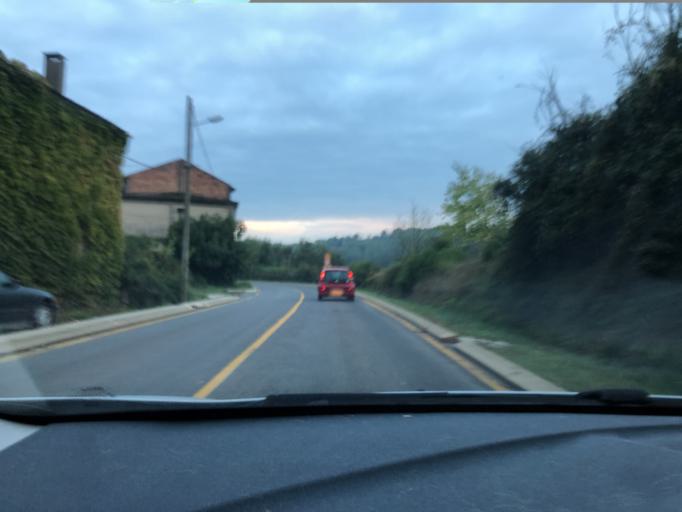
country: FR
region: Languedoc-Roussillon
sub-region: Departement de l'Herault
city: Montferrier-sur-Lez
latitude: 43.6638
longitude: 3.8635
